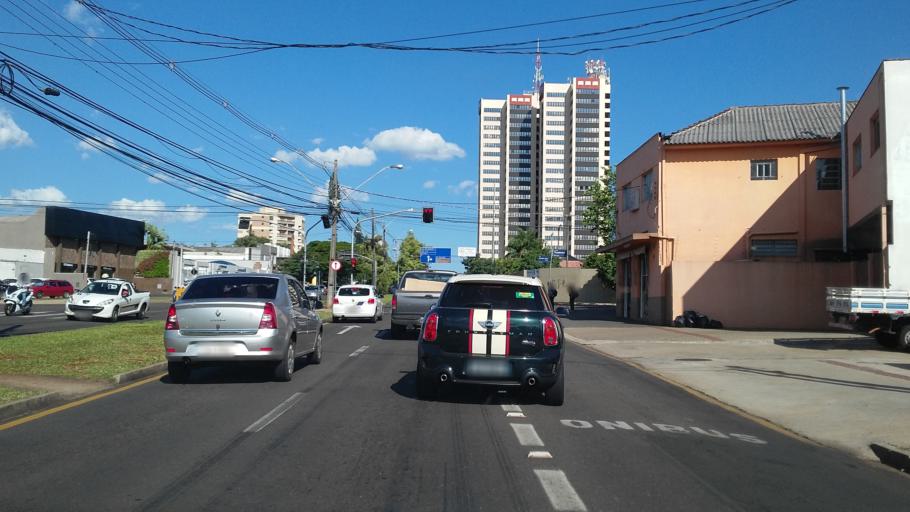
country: BR
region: Parana
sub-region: Londrina
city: Londrina
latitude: -23.3012
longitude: -51.1811
